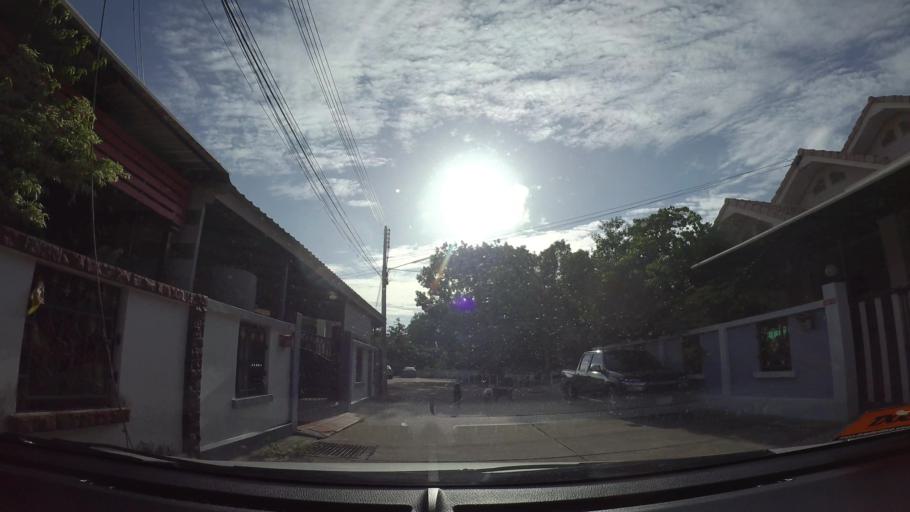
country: TH
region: Chon Buri
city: Sattahip
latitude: 12.6729
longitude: 100.9153
